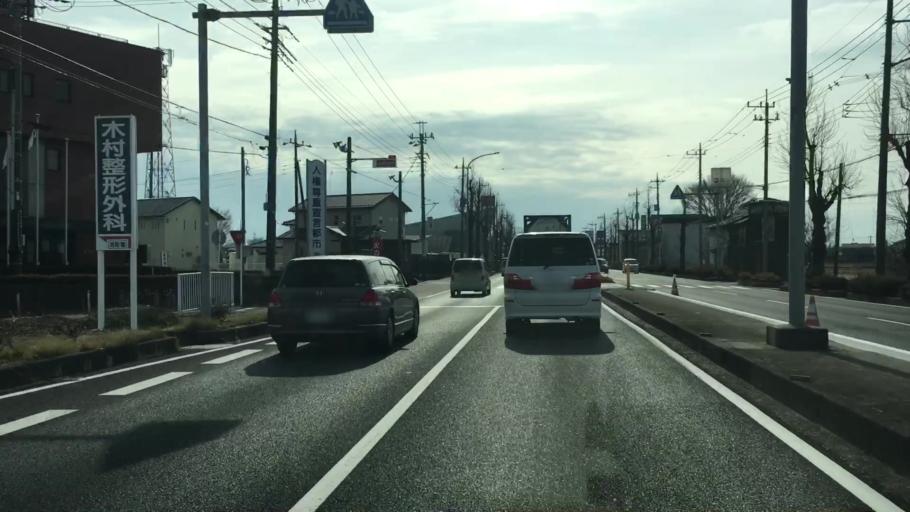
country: JP
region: Saitama
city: Kumagaya
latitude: 36.1683
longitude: 139.3706
